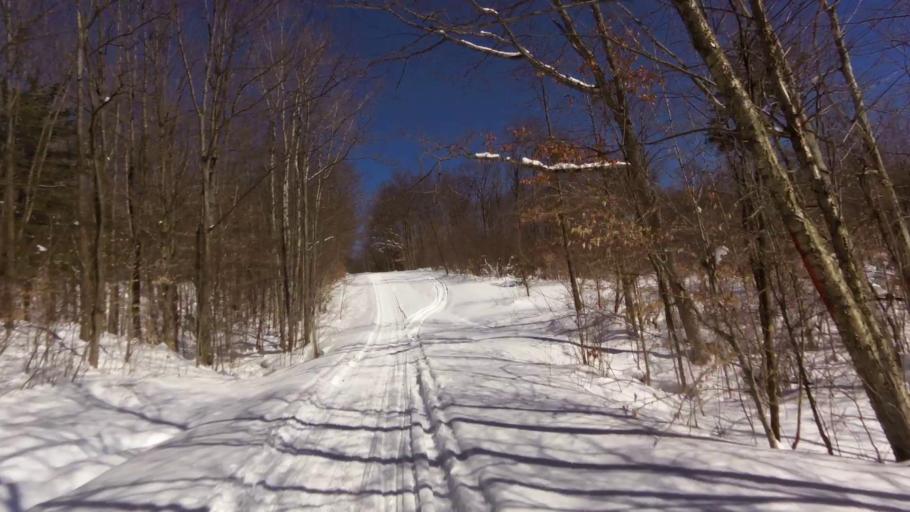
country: US
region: New York
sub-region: Allegany County
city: Cuba
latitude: 42.3168
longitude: -78.2309
